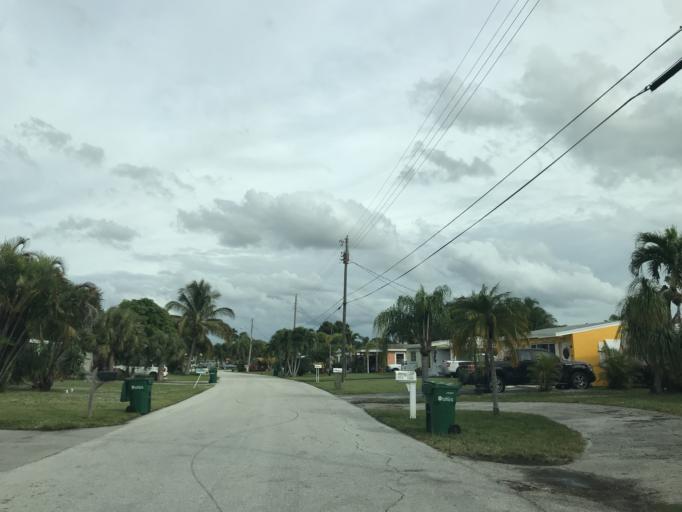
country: US
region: Florida
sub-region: Broward County
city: Margate
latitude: 26.2576
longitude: -80.2054
